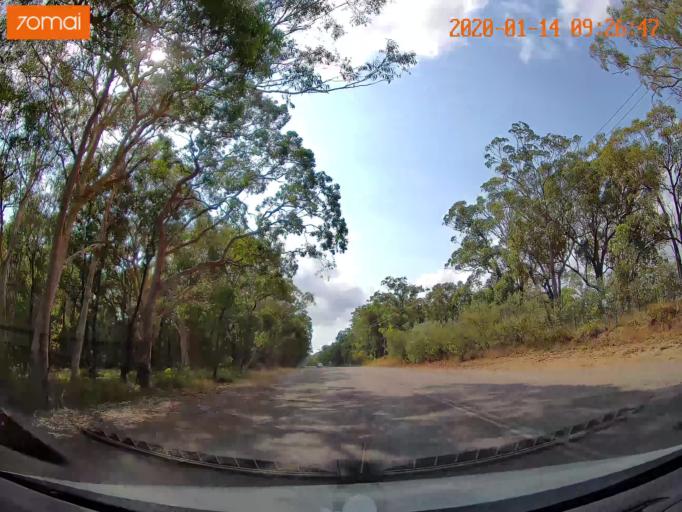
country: AU
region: New South Wales
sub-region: Lake Macquarie Shire
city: Dora Creek
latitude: -33.1175
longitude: 151.5179
